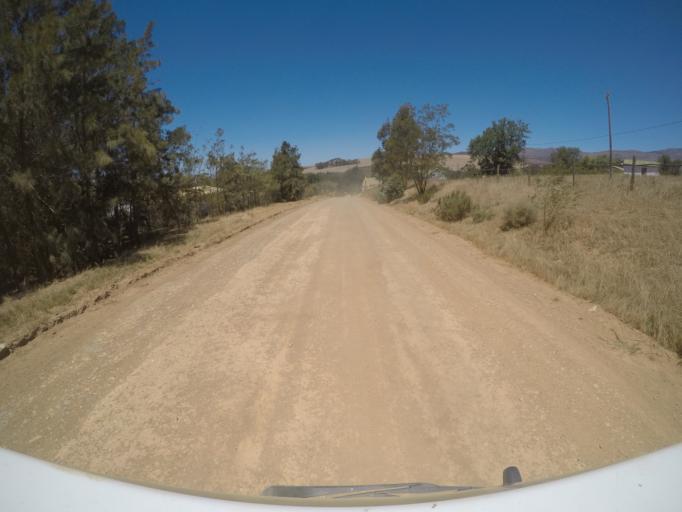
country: ZA
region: Western Cape
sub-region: Overberg District Municipality
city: Grabouw
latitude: -34.0934
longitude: 19.1965
